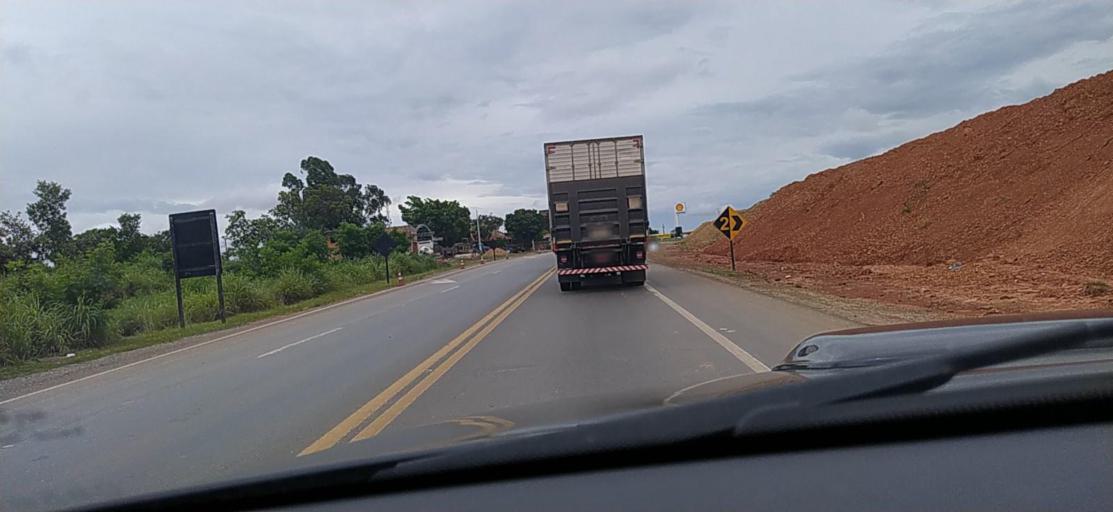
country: BR
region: Minas Gerais
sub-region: Curvelo
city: Curvelo
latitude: -18.7128
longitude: -44.4427
